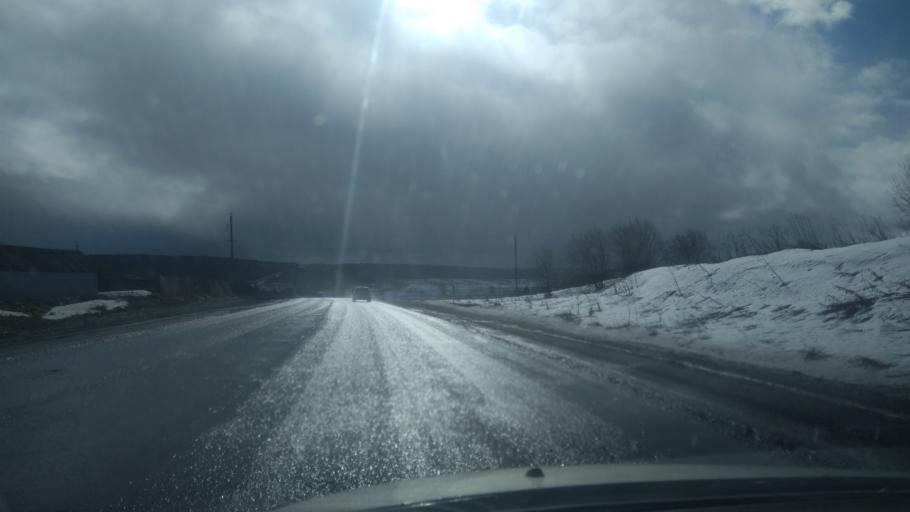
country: RU
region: Perm
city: Kungur
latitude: 57.3763
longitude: 56.9092
